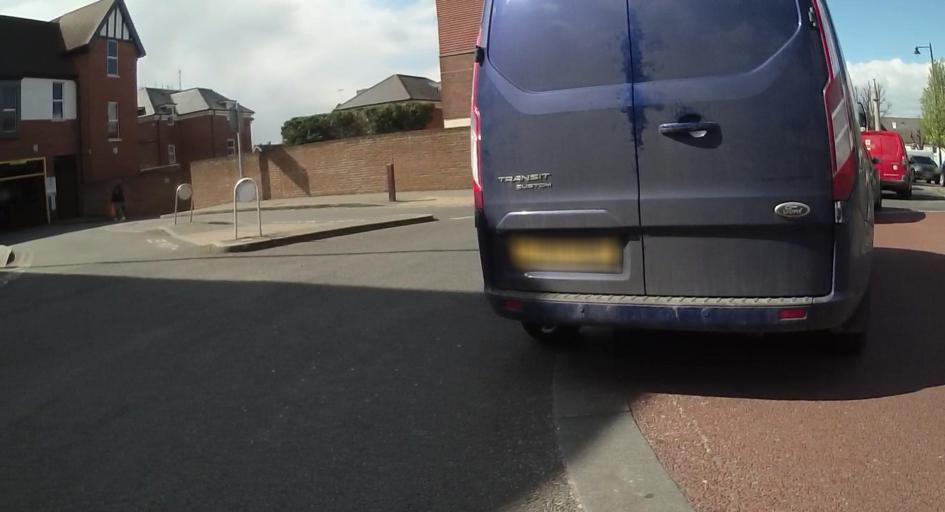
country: GB
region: England
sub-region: Surrey
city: Weybridge
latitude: 51.3732
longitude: -0.4545
